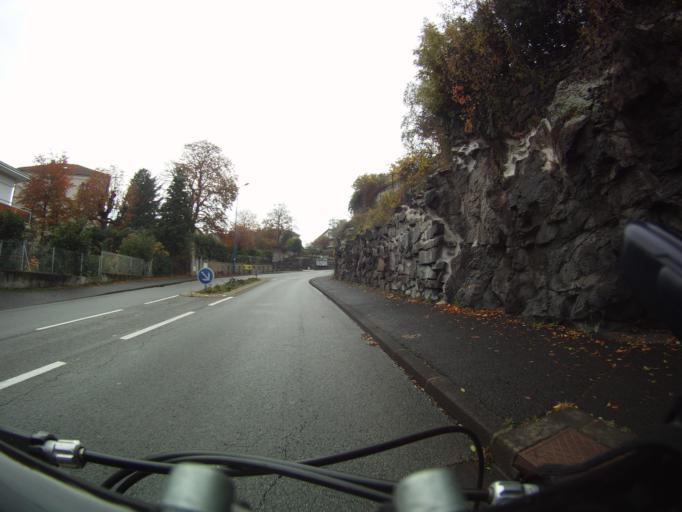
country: FR
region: Auvergne
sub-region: Departement du Puy-de-Dome
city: Aubiere
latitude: 45.7536
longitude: 3.1055
